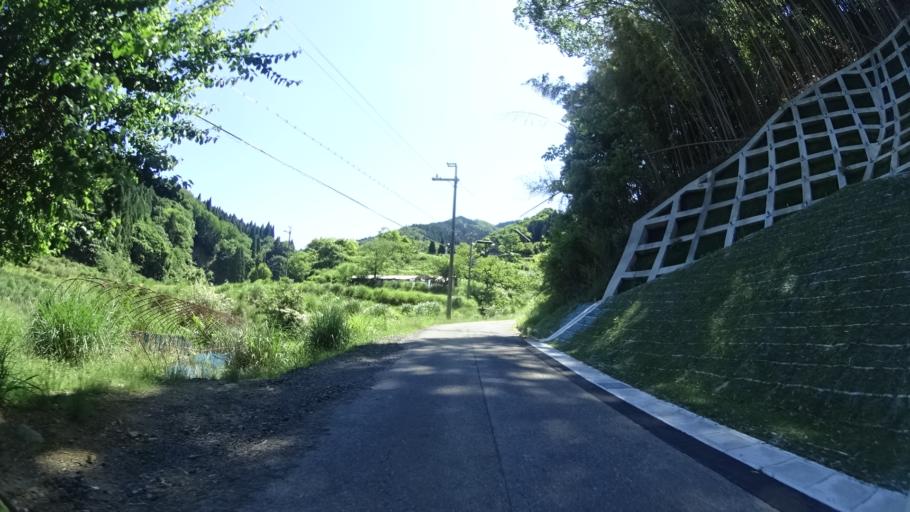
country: JP
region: Kyoto
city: Fukuchiyama
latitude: 35.3837
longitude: 135.0369
